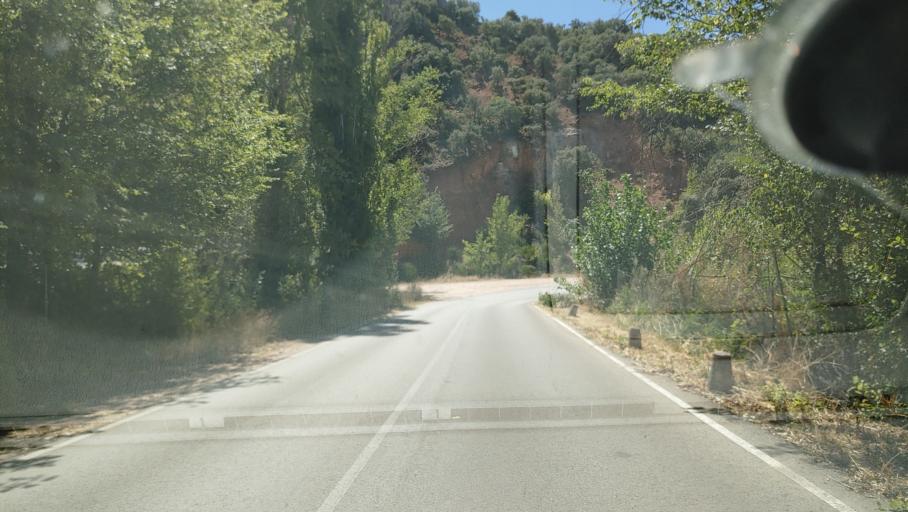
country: ES
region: Castille-La Mancha
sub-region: Provincia de Ciudad Real
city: Ruidera
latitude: 38.9606
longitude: -2.8577
